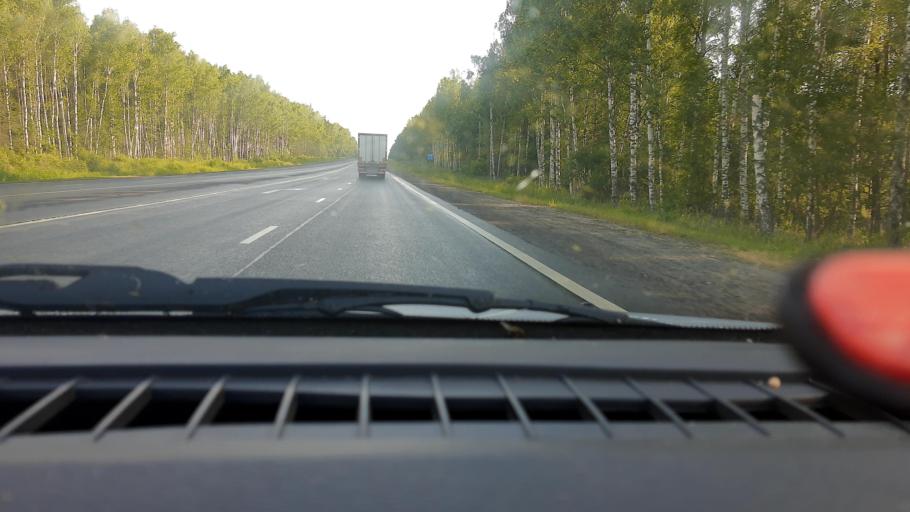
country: RU
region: Nizjnij Novgorod
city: Arzamas
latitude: 55.4968
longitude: 43.8917
